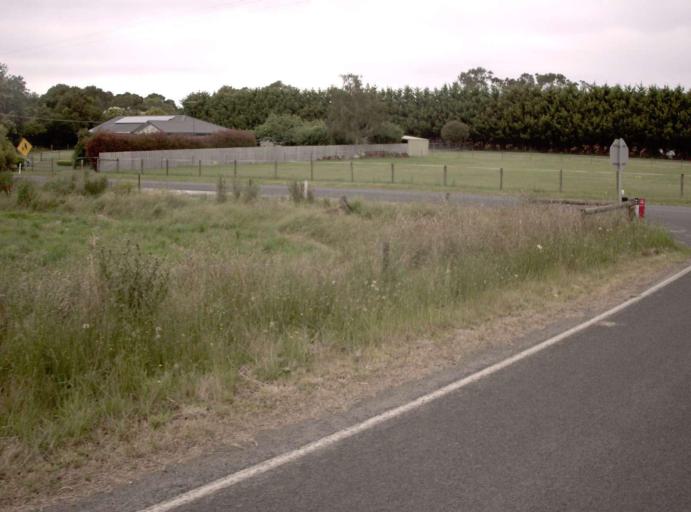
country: AU
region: Victoria
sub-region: Baw Baw
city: Warragul
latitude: -38.4964
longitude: 145.9520
